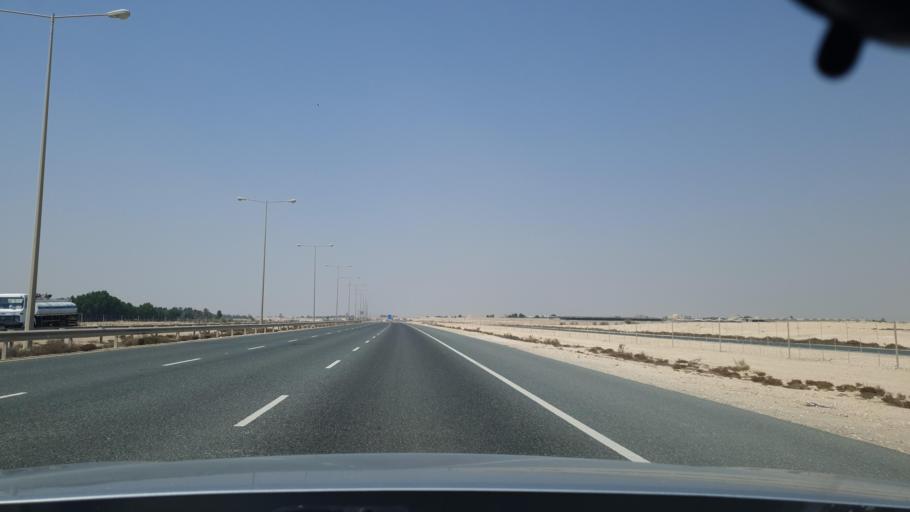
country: QA
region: Al Khawr
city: Al Khawr
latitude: 25.7760
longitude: 51.4086
